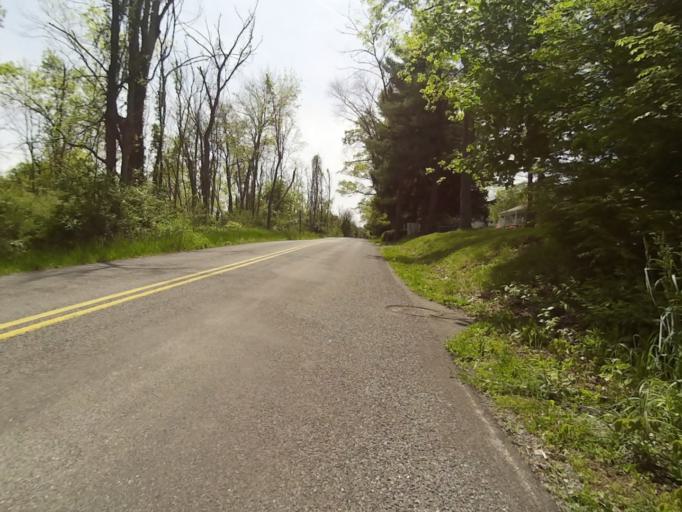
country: US
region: Pennsylvania
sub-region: Centre County
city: Houserville
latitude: 40.8815
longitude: -77.8656
